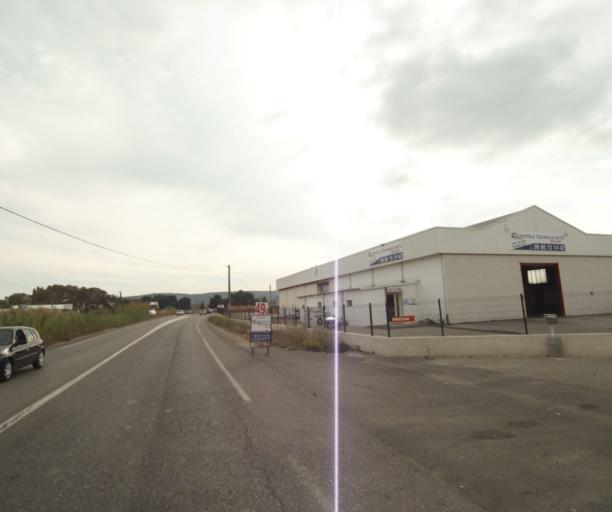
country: FR
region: Provence-Alpes-Cote d'Azur
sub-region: Departement des Bouches-du-Rhone
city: Marignane
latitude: 43.3968
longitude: 5.1978
